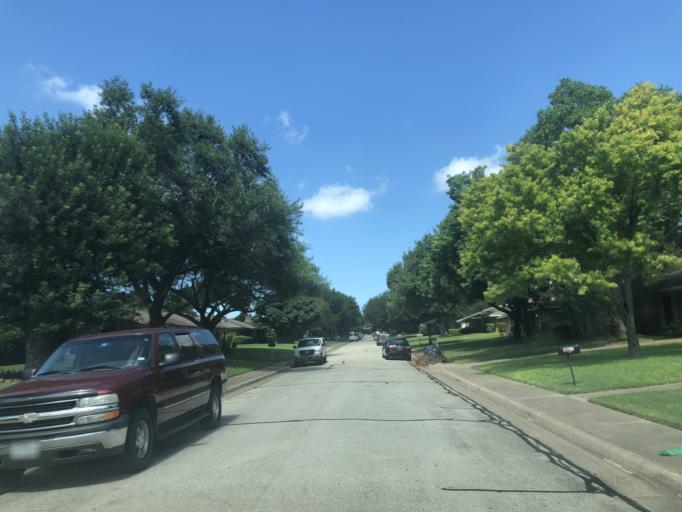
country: US
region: Texas
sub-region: Dallas County
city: Duncanville
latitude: 32.6496
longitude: -96.9304
